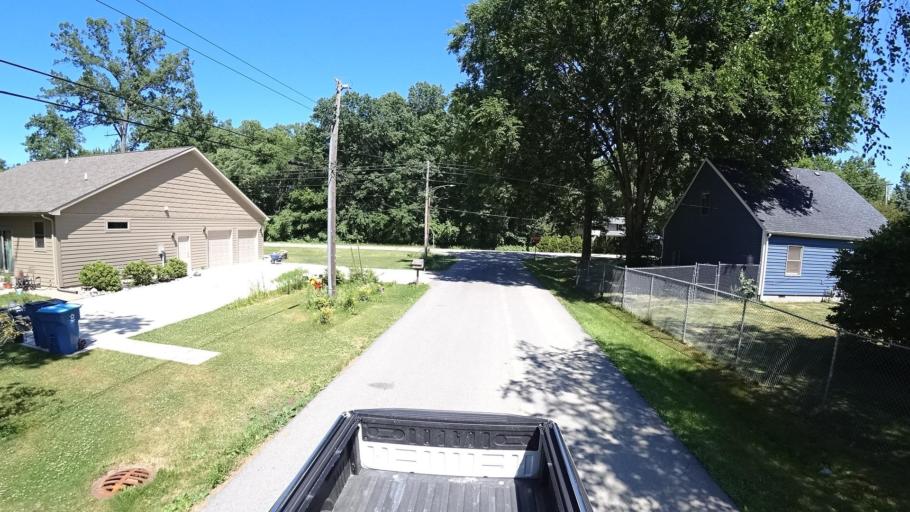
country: US
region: Indiana
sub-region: Porter County
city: Porter
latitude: 41.6028
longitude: -87.0820
